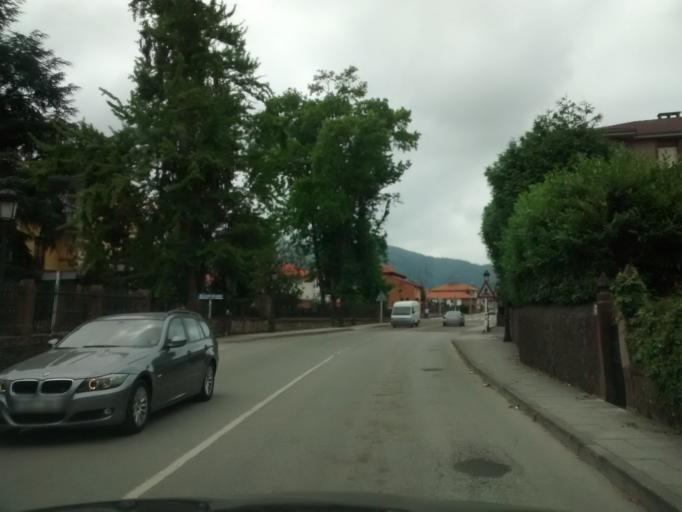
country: ES
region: Cantabria
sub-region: Provincia de Cantabria
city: Cabezon de la Sal
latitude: 43.3039
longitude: -4.2377
